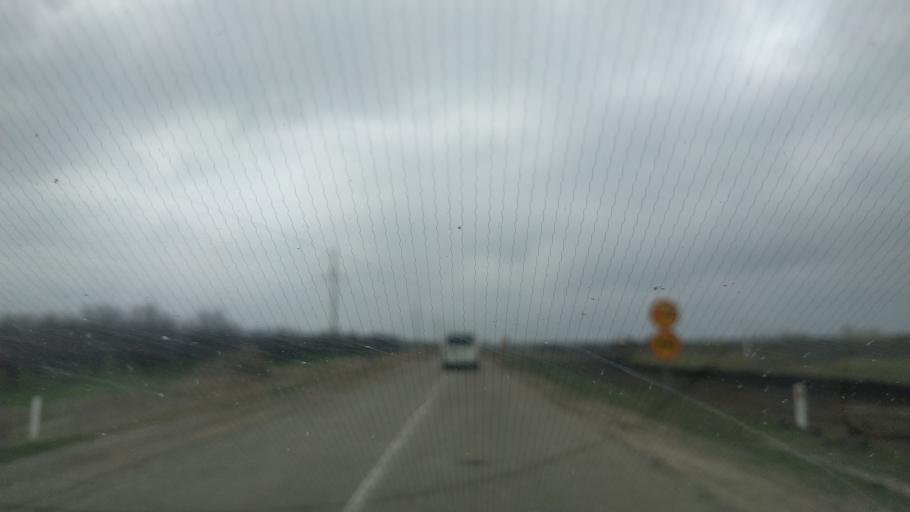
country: MD
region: Gagauzia
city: Bugeac
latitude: 46.3303
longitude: 28.7341
